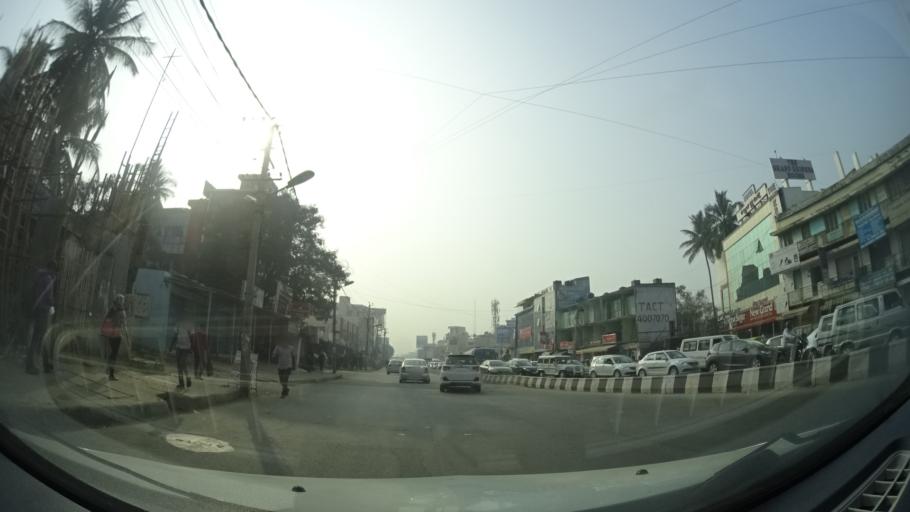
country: IN
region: Karnataka
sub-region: Bangalore Urban
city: Bangalore
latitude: 12.9250
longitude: 77.6182
